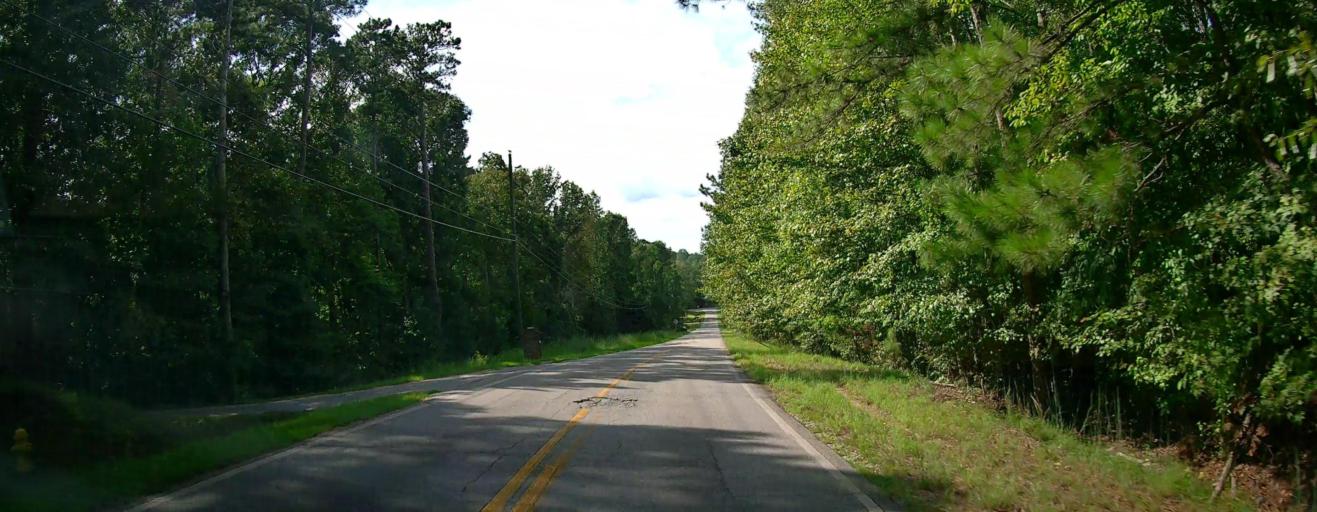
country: US
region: Alabama
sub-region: Russell County
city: Phenix City
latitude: 32.6049
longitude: -84.9776
